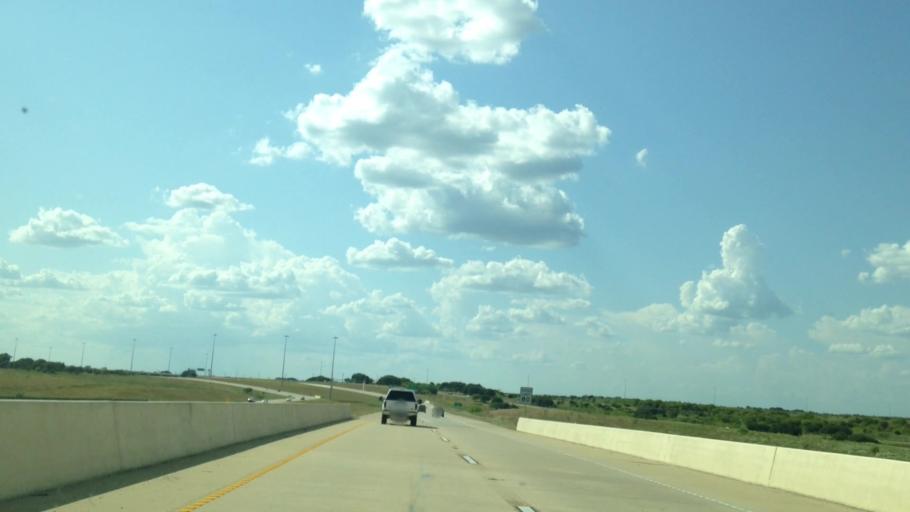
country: US
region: Texas
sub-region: Travis County
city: Onion Creek
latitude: 30.1073
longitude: -97.7899
